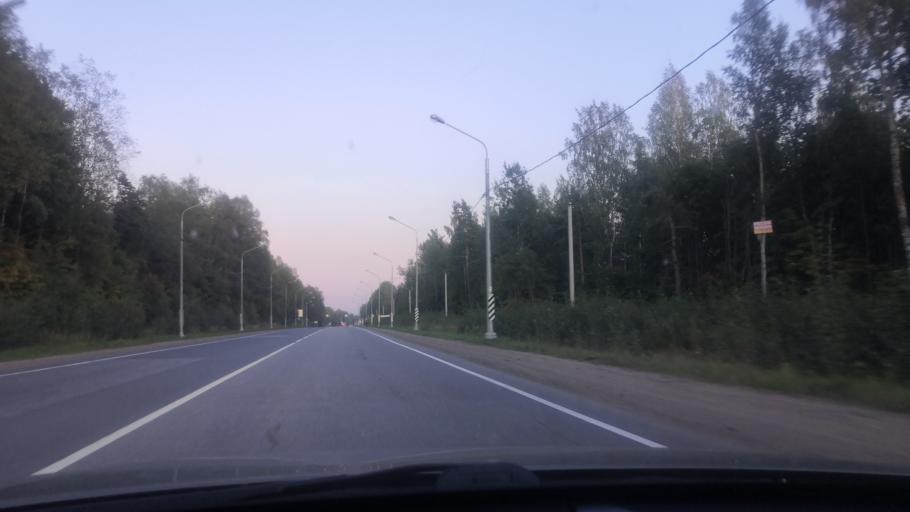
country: RU
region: St.-Petersburg
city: Beloostrov
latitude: 60.1953
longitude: 30.0675
